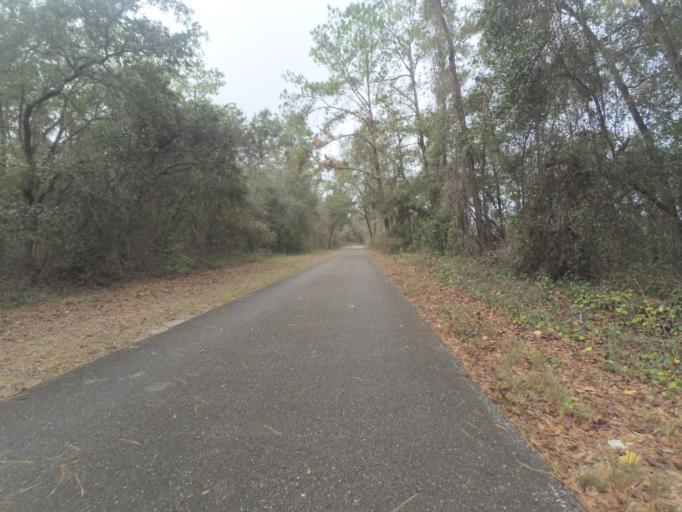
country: US
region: Florida
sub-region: Alachua County
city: Gainesville
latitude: 29.6131
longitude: -82.2587
